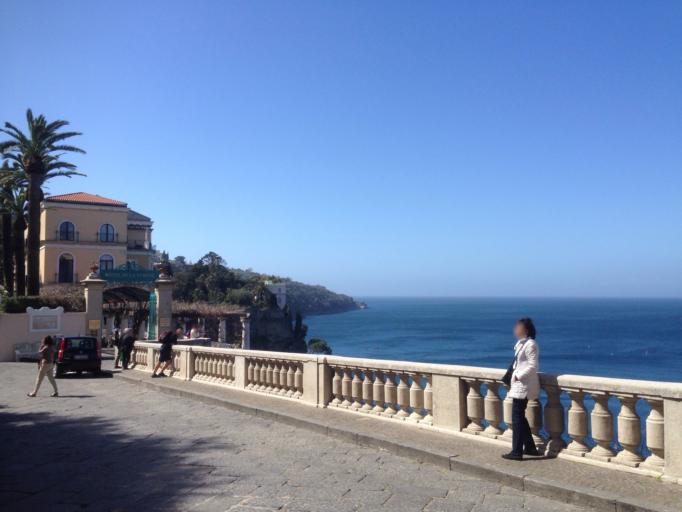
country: IT
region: Campania
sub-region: Provincia di Napoli
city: Sorrento
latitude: 40.6275
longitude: 14.3714
